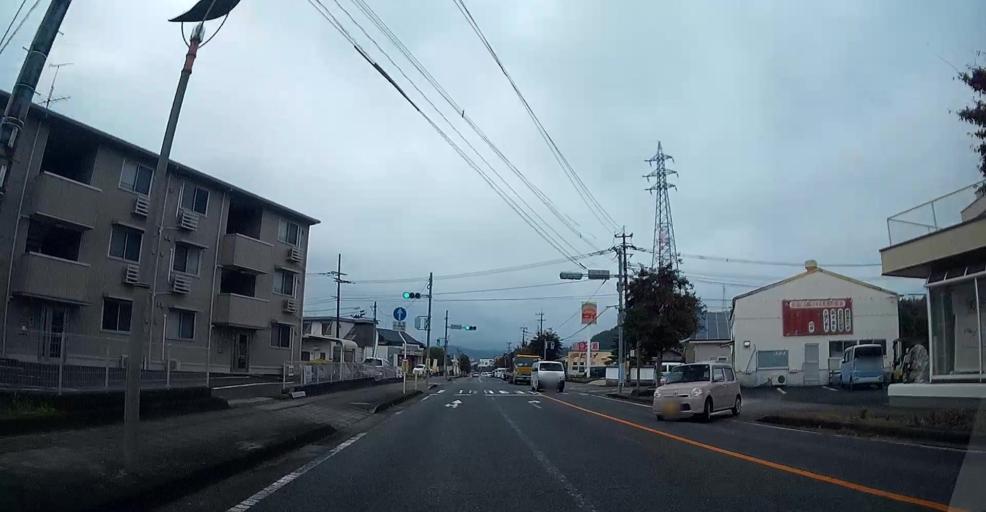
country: JP
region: Kumamoto
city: Matsubase
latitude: 32.6557
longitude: 130.6844
